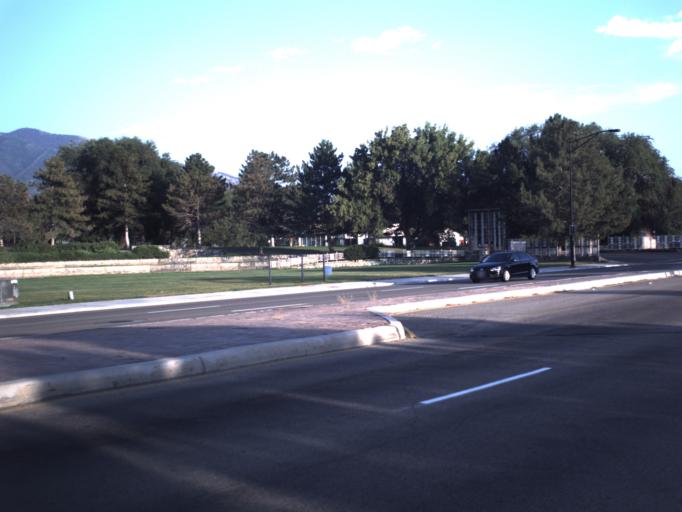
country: US
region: Utah
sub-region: Salt Lake County
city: Sandy City
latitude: 40.5675
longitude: -111.8910
